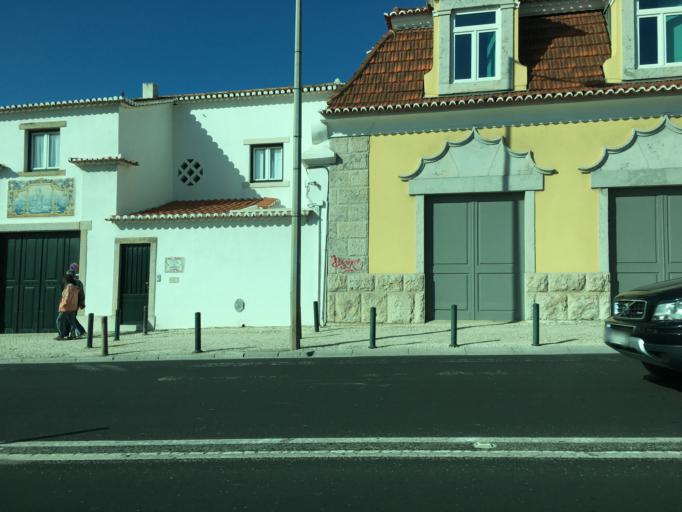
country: PT
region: Lisbon
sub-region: Cascais
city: Estoril
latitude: 38.7040
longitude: -9.4022
